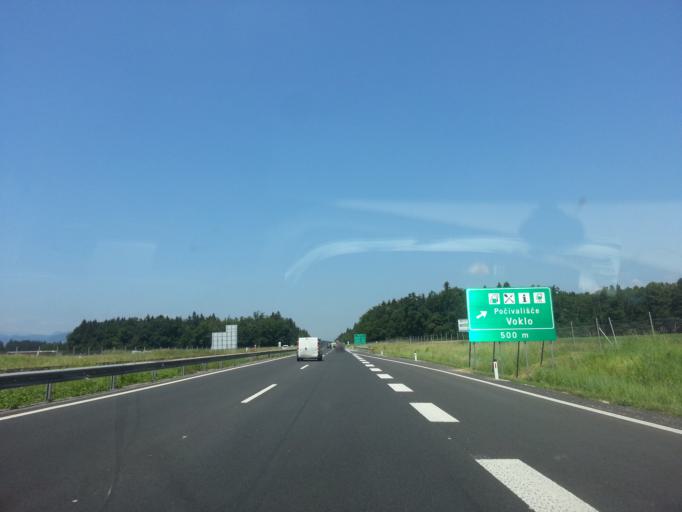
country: SI
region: Sencur
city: Sencur
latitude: 46.2214
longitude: 14.4342
